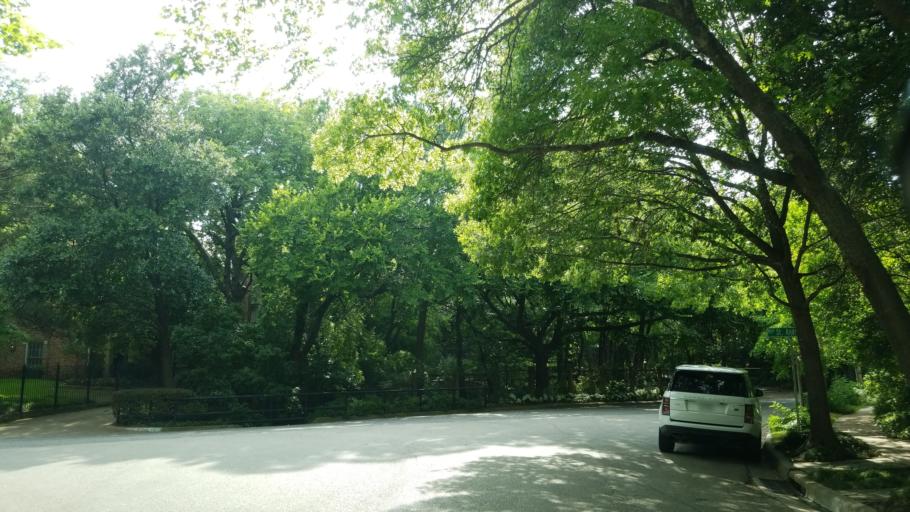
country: US
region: Texas
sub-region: Dallas County
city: University Park
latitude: 32.8419
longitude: -96.8030
